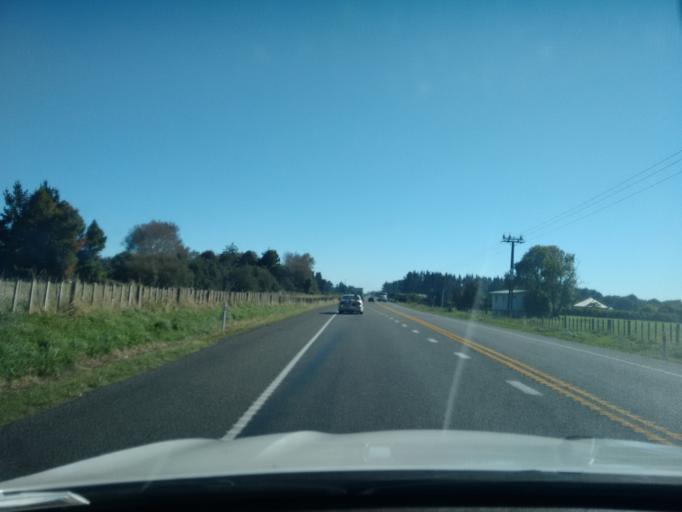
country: NZ
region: Taranaki
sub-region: South Taranaki District
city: Eltham
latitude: -39.2341
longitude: 174.2432
